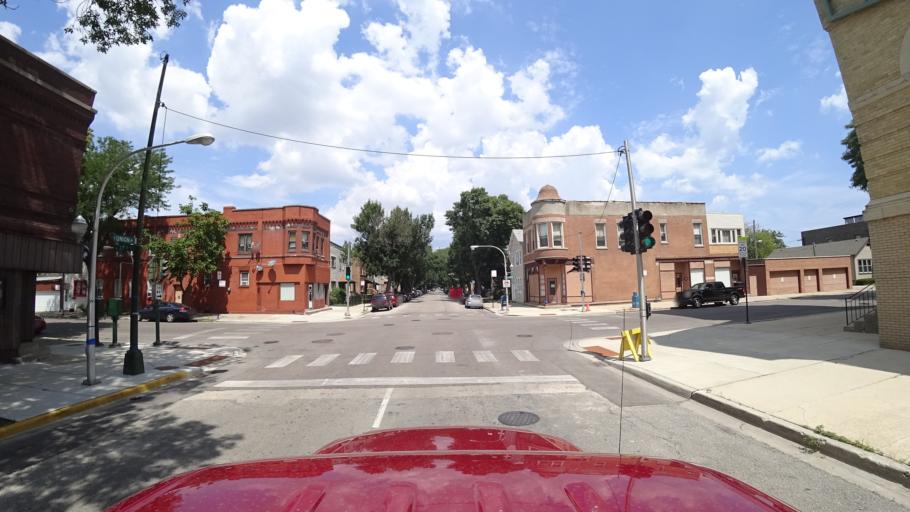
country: US
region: Illinois
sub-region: Cook County
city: Chicago
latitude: 41.8269
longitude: -87.6435
